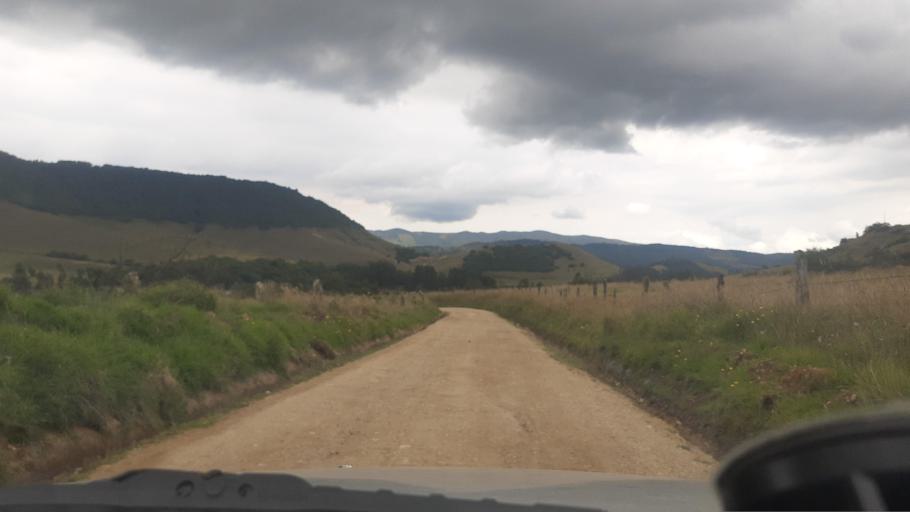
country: CO
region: Cundinamarca
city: Suesca
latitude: 5.1519
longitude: -73.7923
